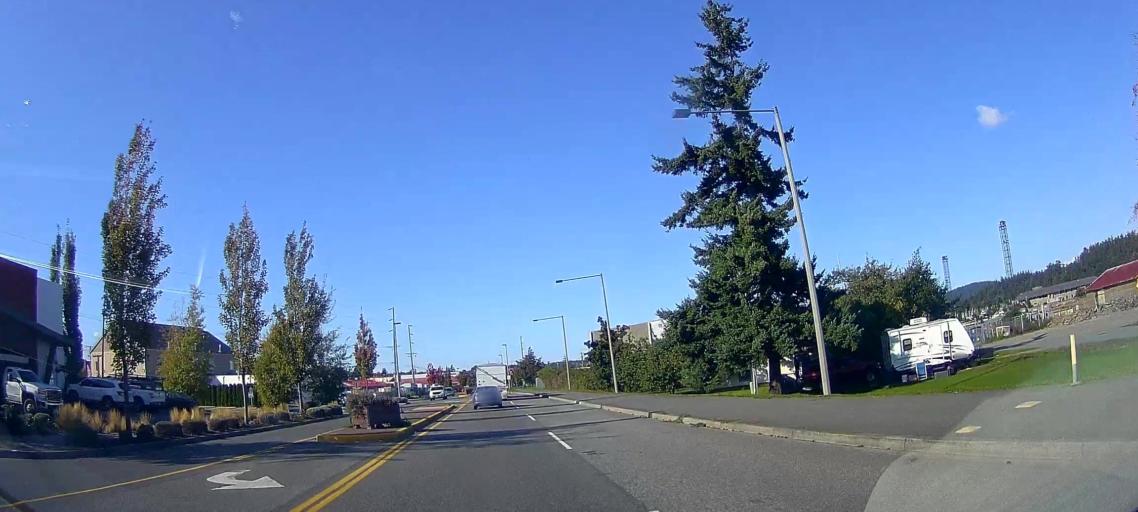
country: US
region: Washington
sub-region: Skagit County
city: Anacortes
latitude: 48.5054
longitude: -122.6099
